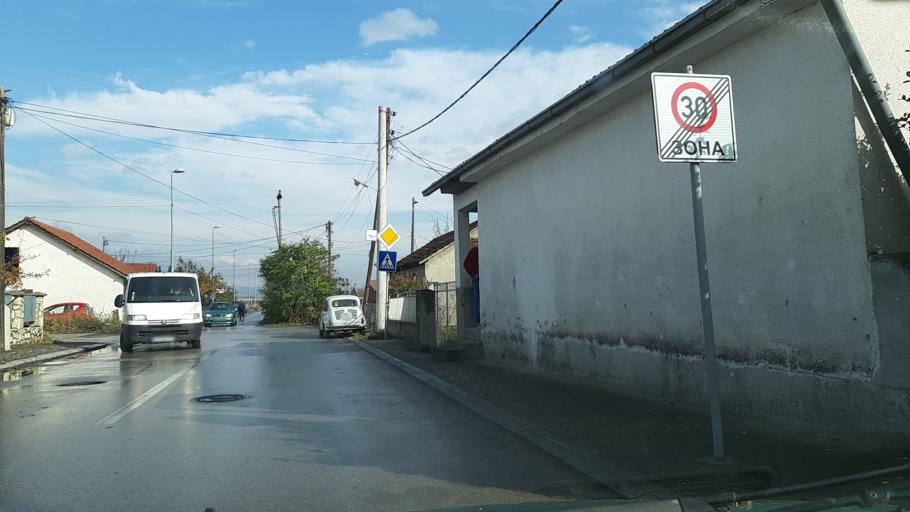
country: MK
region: Kisela Voda
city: Kisela Voda
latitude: 41.9814
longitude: 21.4904
